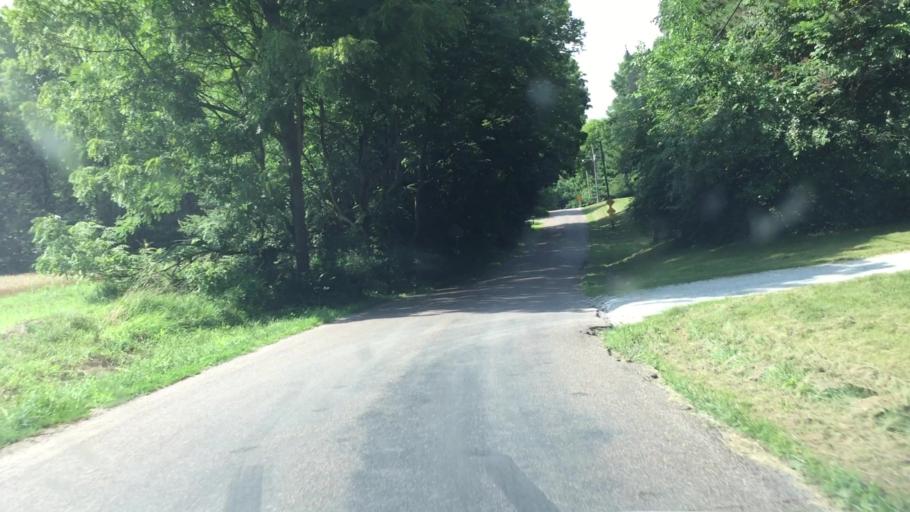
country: US
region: Illinois
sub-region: Hancock County
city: Nauvoo
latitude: 40.5391
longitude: -91.3759
